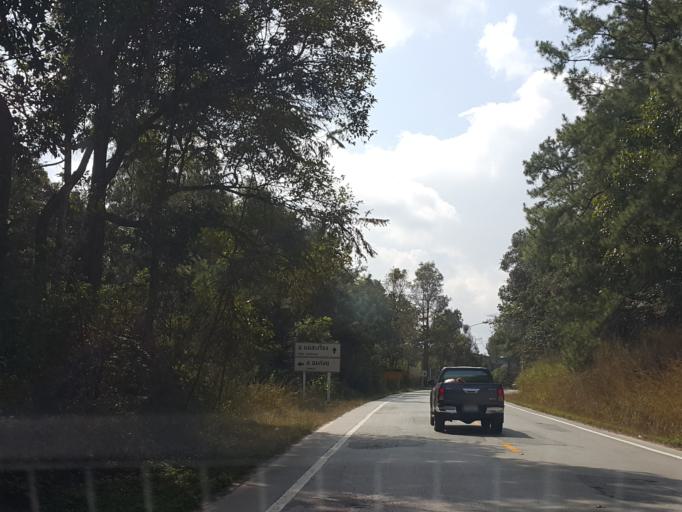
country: TH
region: Chiang Mai
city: Hot
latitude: 18.1425
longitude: 98.3756
